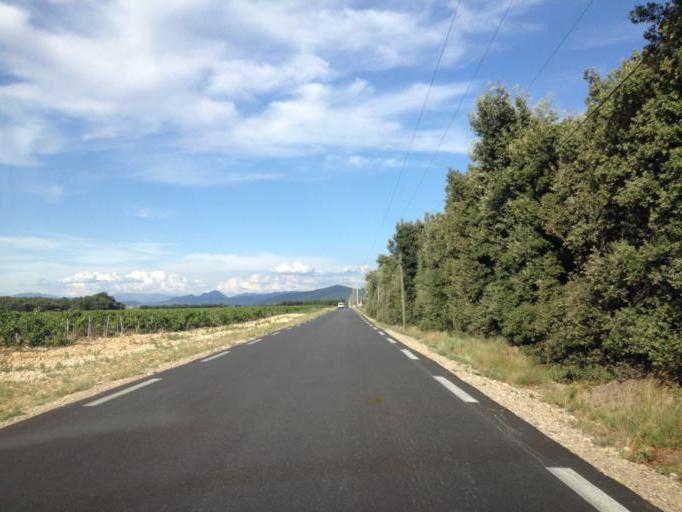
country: FR
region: Provence-Alpes-Cote d'Azur
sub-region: Departement du Vaucluse
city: Violes
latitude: 44.1863
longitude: 4.9576
